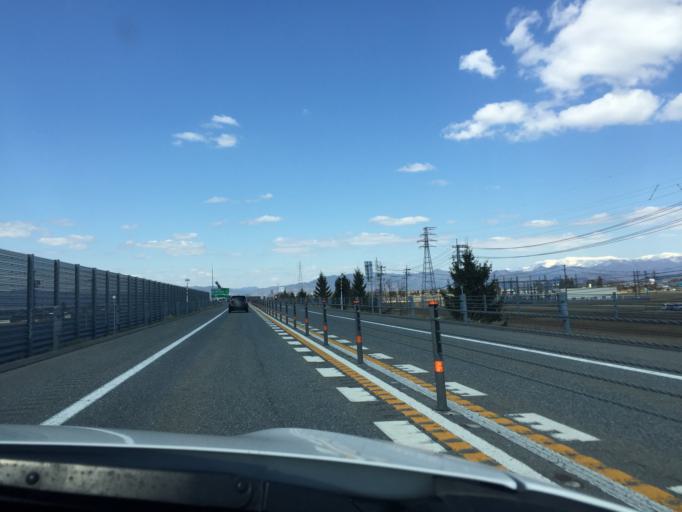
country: JP
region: Yamagata
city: Yonezawa
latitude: 37.9636
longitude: 140.1206
